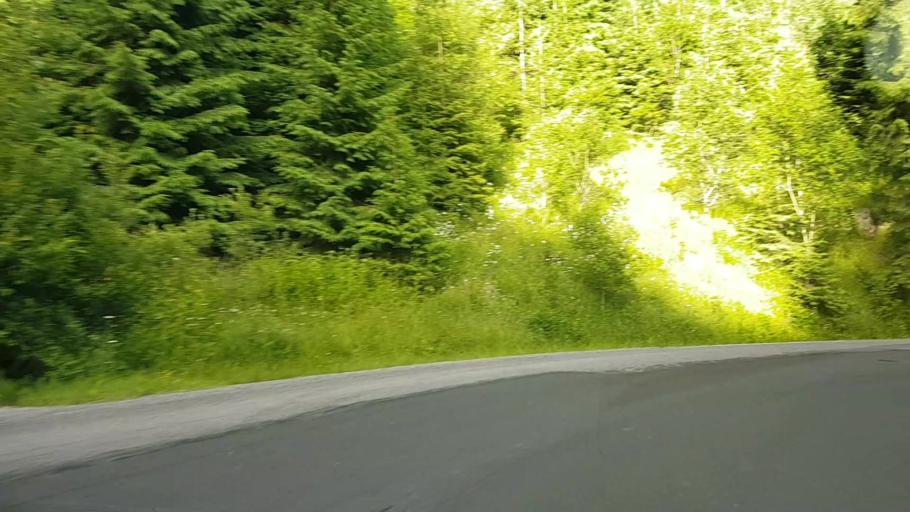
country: RO
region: Harghita
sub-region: Municipiul Gheorgheni
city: Gheorgheni
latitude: 46.7739
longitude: 25.7108
